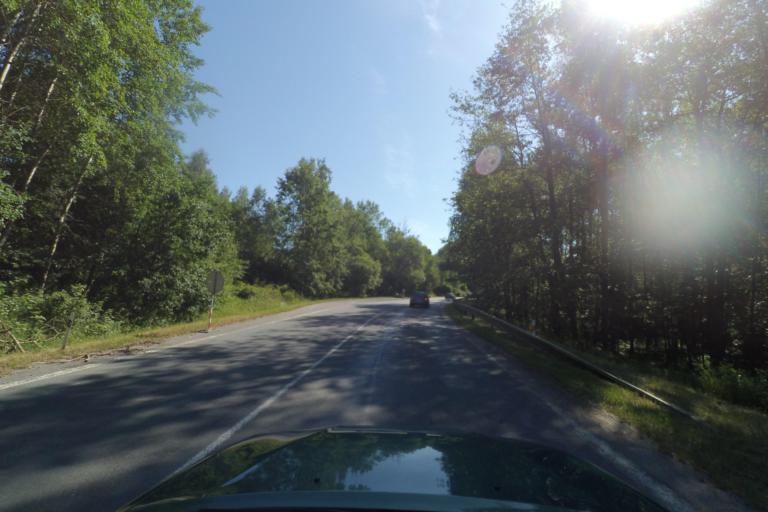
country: CZ
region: Karlovarsky
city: Nova Role
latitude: 50.2400
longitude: 12.7784
